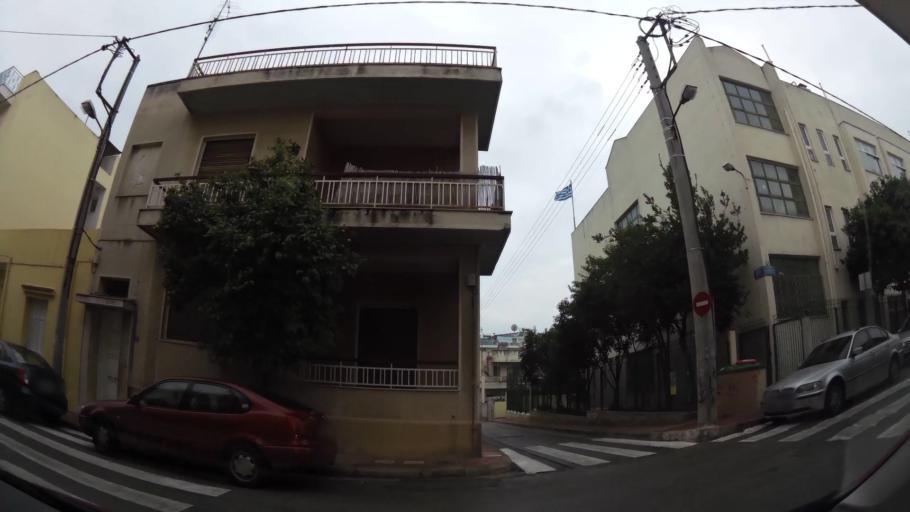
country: GR
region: Attica
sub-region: Nomarchia Athinas
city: Agioi Anargyroi
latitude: 38.0357
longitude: 23.7244
